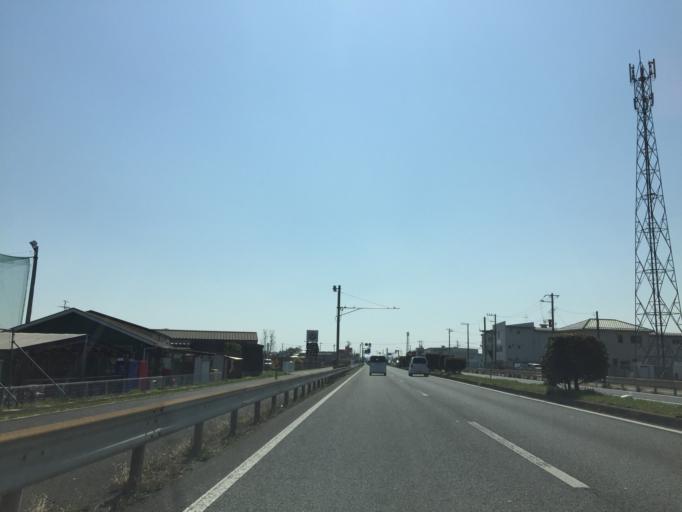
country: JP
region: Saitama
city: Kamifukuoka
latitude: 35.8856
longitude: 139.5319
